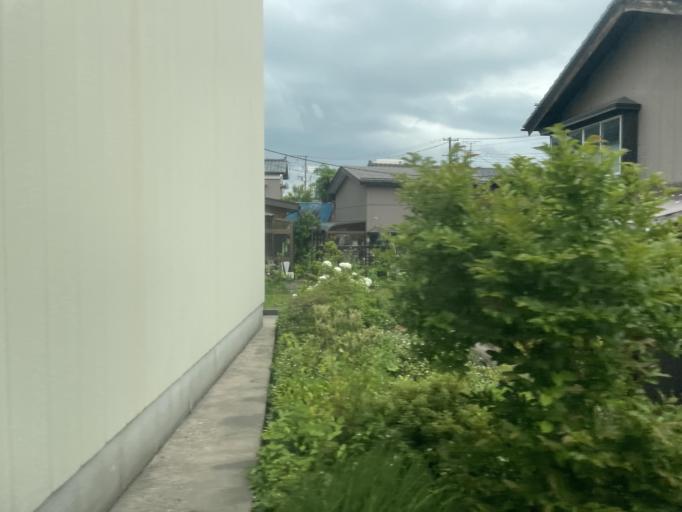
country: JP
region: Niigata
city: Tsubame
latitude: 37.6678
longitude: 138.9254
